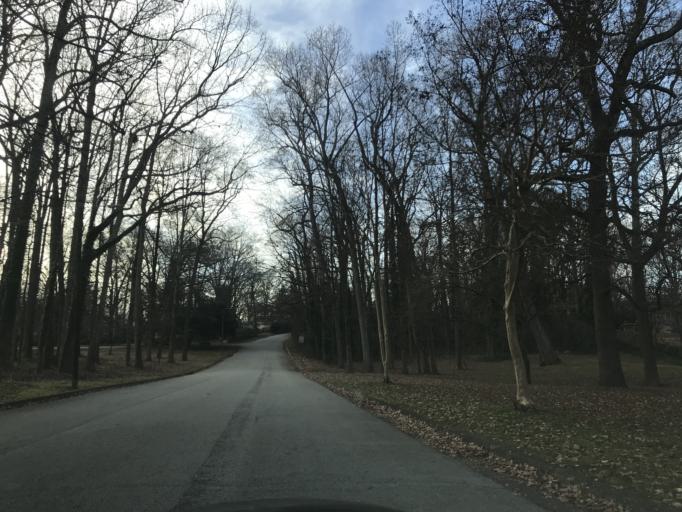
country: US
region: North Carolina
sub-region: Wake County
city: Raleigh
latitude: 35.7987
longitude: -78.6140
